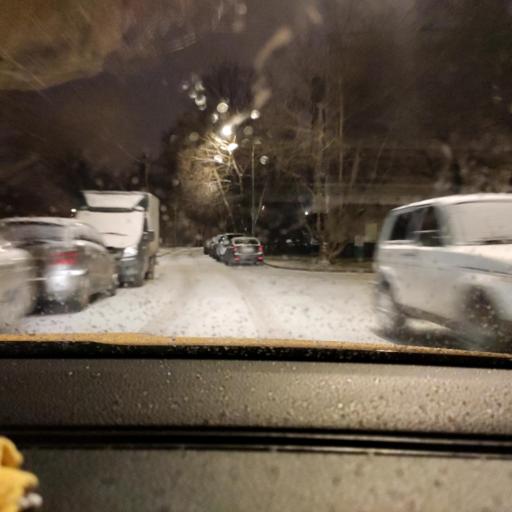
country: RU
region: Moscow
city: Strogino
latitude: 55.8529
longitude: 37.3866
